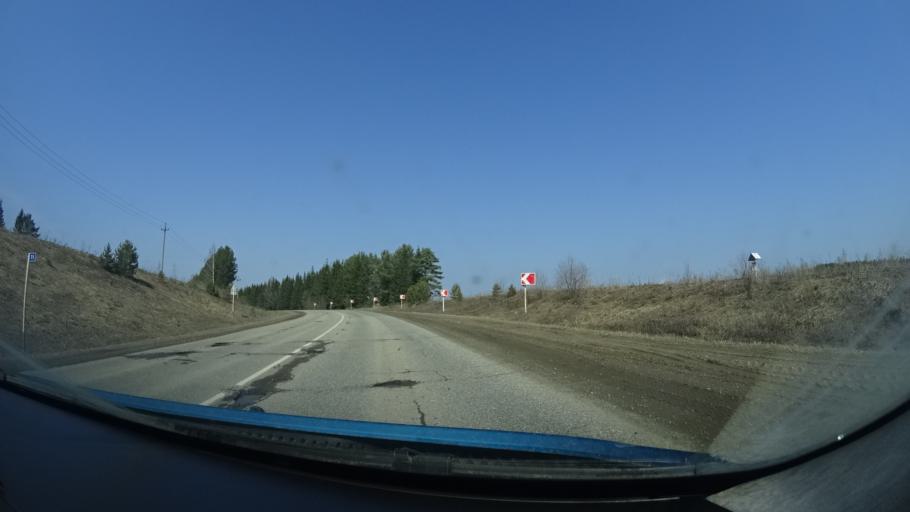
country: RU
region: Perm
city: Osa
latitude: 57.3153
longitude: 55.6236
